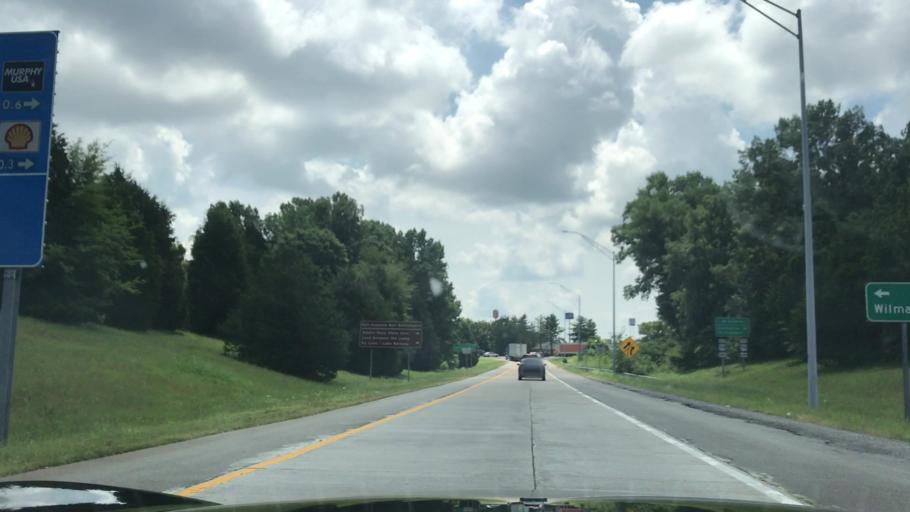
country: US
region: Tennessee
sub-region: Montgomery County
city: Clarksville
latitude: 36.6008
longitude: -87.2851
